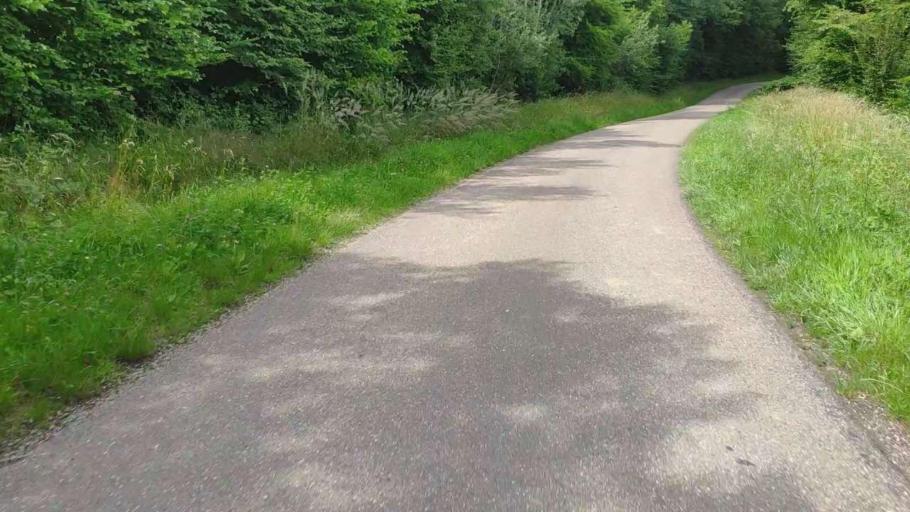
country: FR
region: Franche-Comte
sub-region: Departement du Jura
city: Chaussin
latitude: 46.8861
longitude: 5.4041
